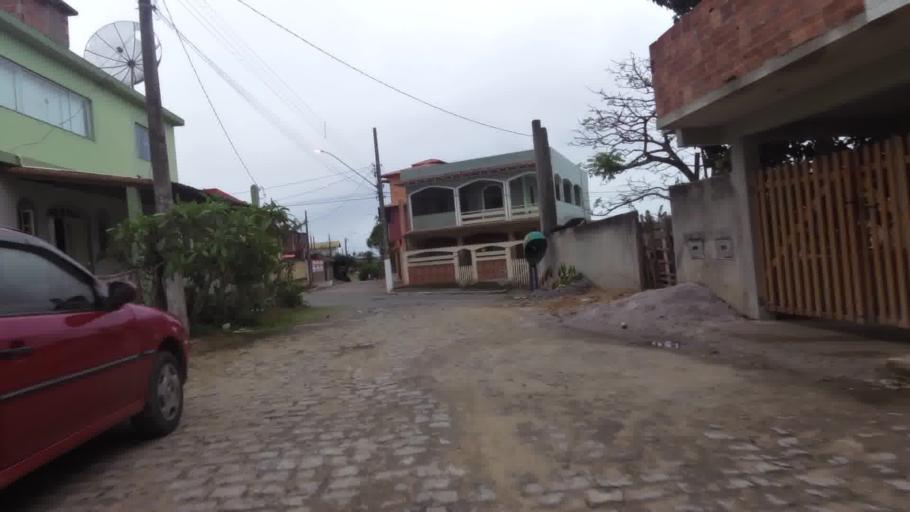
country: BR
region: Espirito Santo
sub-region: Marataizes
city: Marataizes
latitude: -21.0442
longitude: -40.8337
